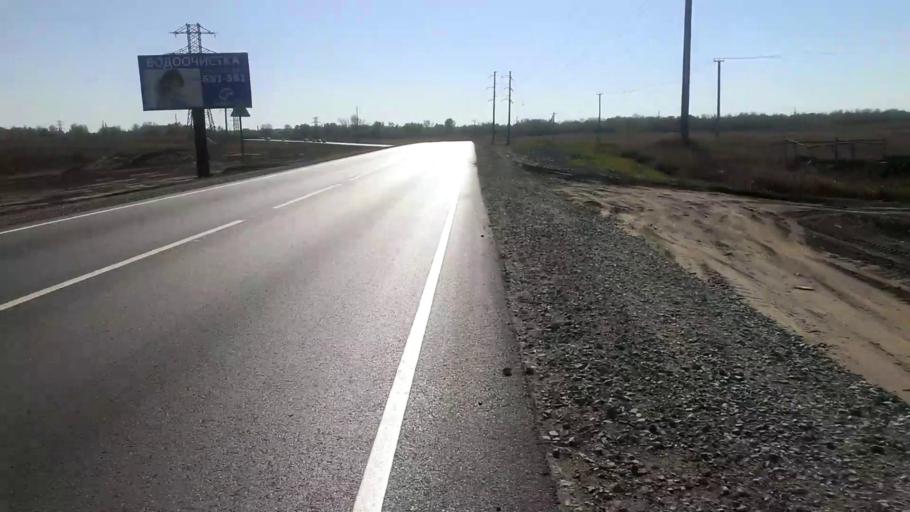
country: RU
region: Altai Krai
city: Sannikovo
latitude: 53.3347
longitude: 83.9381
